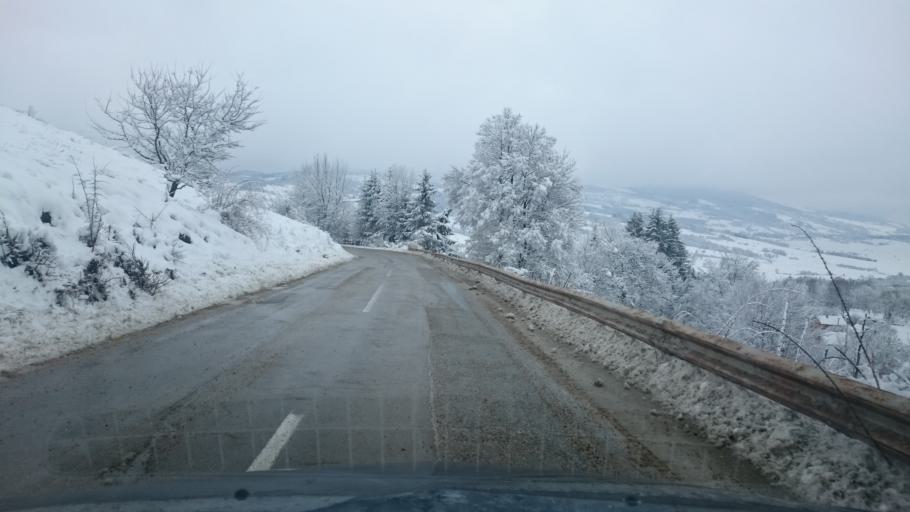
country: BA
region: Republika Srpska
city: Zivinice
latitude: 44.5145
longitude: 17.3088
